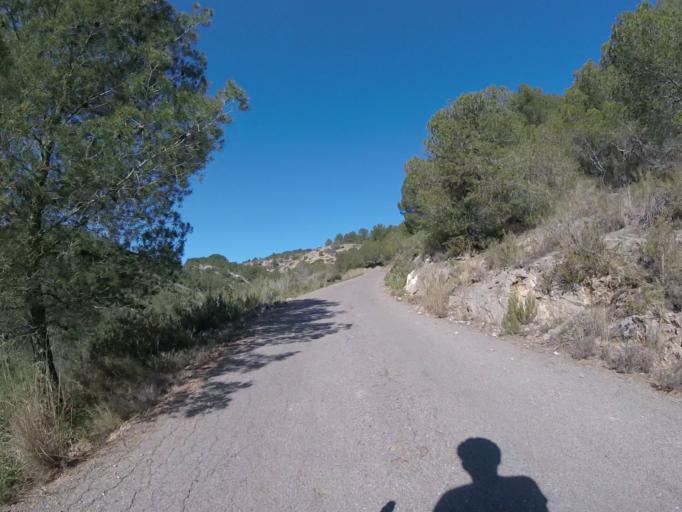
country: ES
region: Valencia
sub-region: Provincia de Castello
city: Benicassim
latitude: 40.0779
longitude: 0.0921
